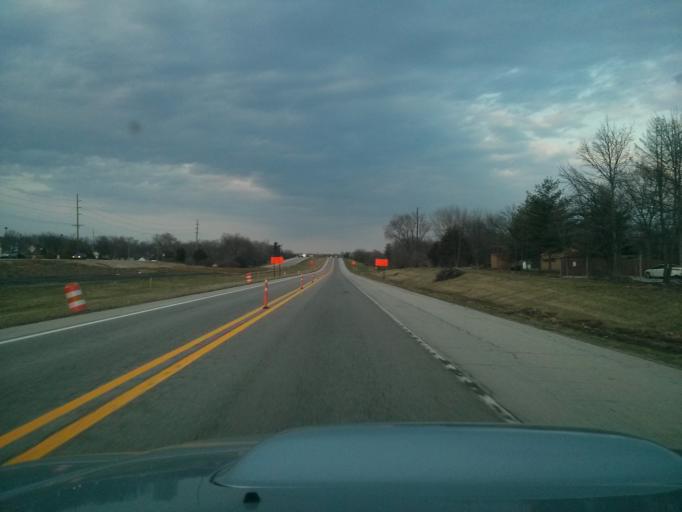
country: US
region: Indiana
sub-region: Hamilton County
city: Carmel
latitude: 39.9857
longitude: -86.1387
